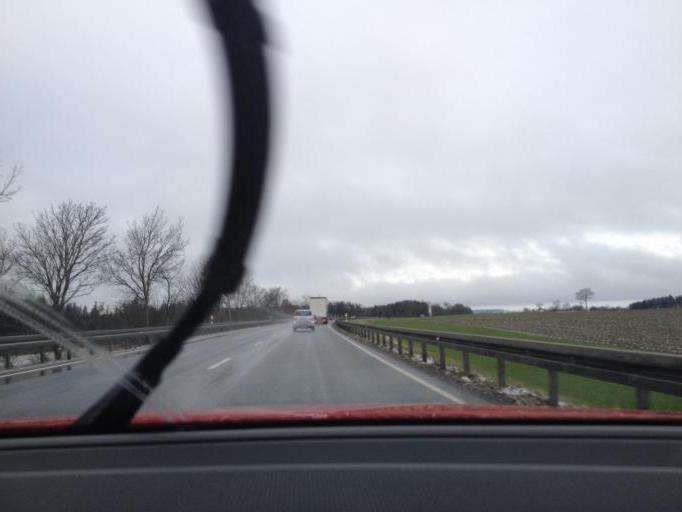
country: DE
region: Bavaria
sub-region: Upper Franconia
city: Rehau
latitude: 50.2689
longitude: 12.0050
